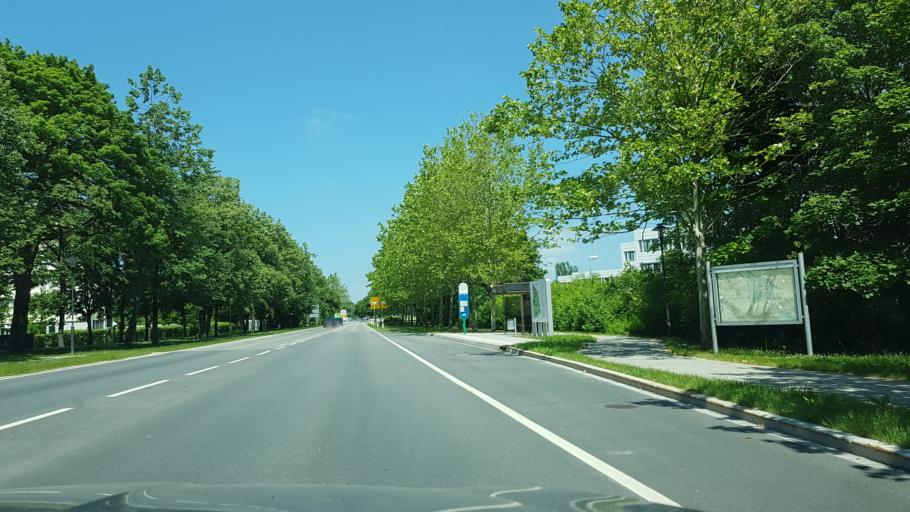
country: DE
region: Bavaria
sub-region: Upper Bavaria
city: Aschheim
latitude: 48.1477
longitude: 11.6854
